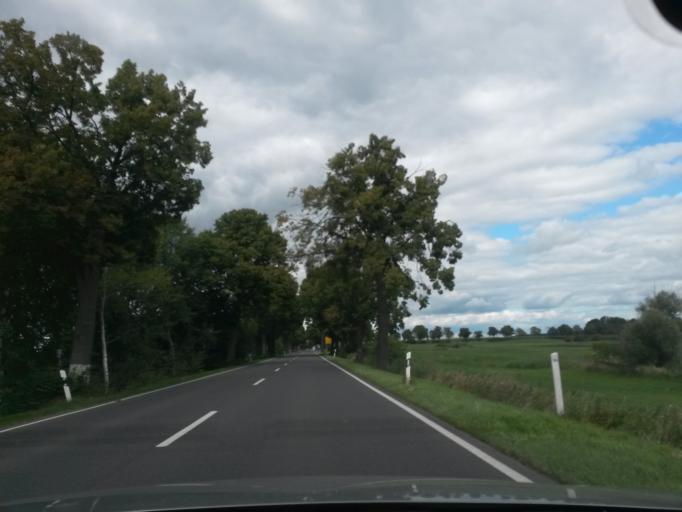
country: DE
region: Brandenburg
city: Angermunde
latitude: 52.9739
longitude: 13.9683
